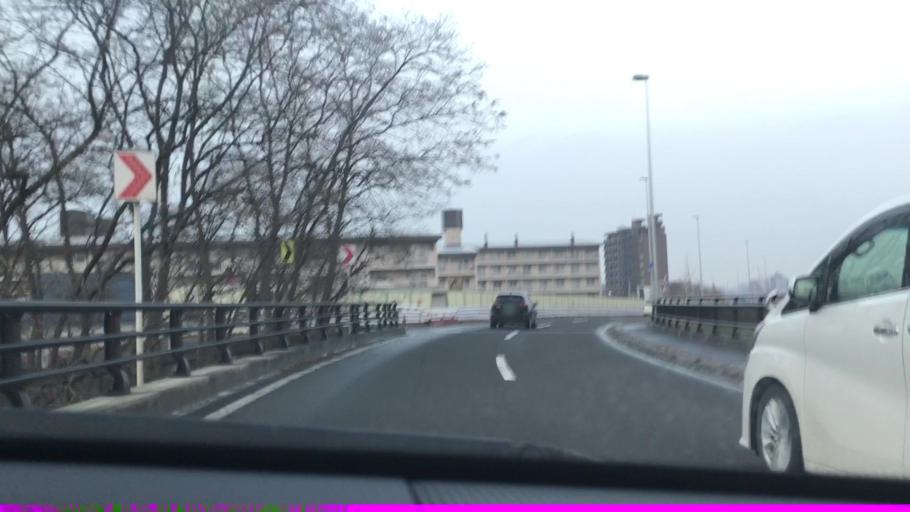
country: JP
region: Hokkaido
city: Sapporo
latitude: 43.0216
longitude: 141.3505
